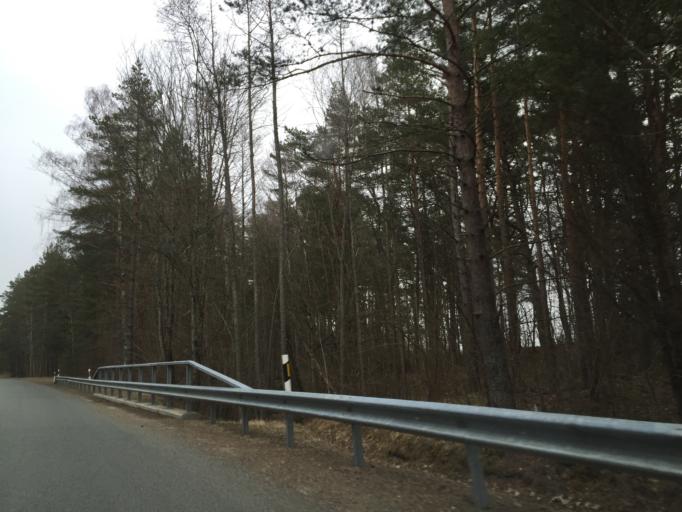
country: LV
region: Salacgrivas
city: Ainazi
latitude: 58.0195
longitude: 24.4537
